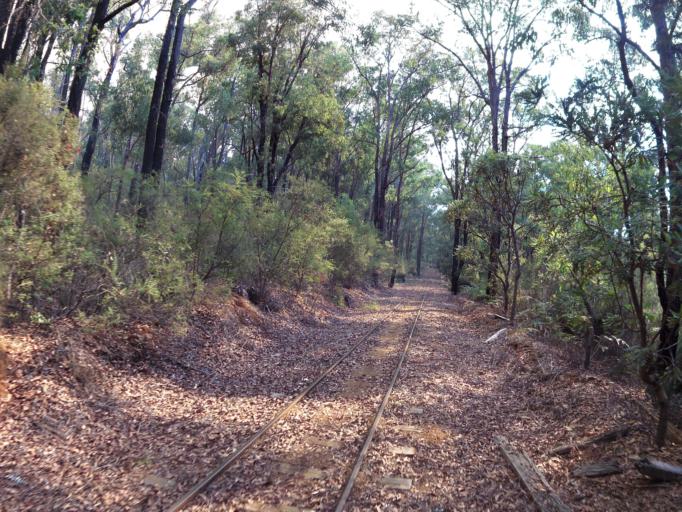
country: AU
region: Western Australia
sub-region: Waroona
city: Waroona
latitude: -32.7377
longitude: 116.1229
